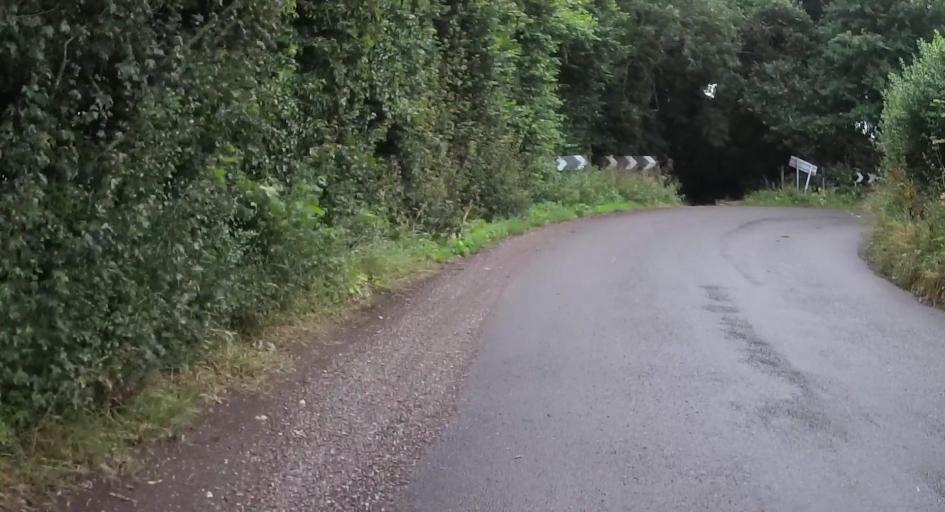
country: GB
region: England
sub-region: Hampshire
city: Andover
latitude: 51.2439
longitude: -1.4113
